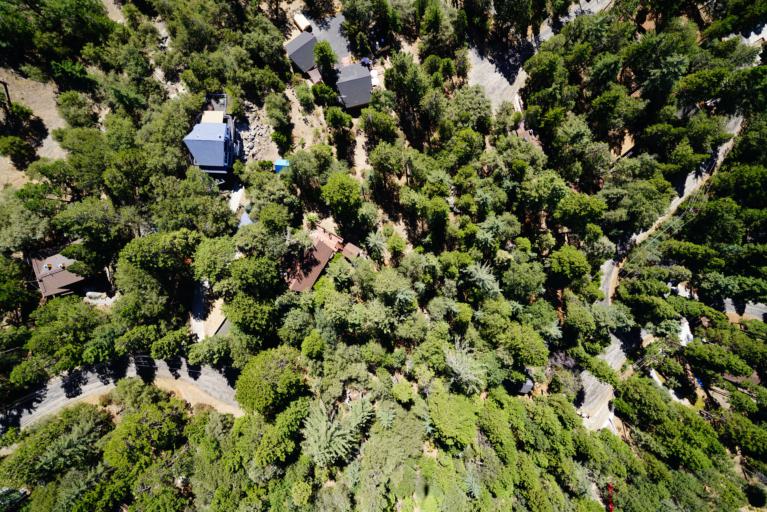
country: US
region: California
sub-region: Riverside County
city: Idyllwild-Pine Cove
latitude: 33.7524
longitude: -116.7493
